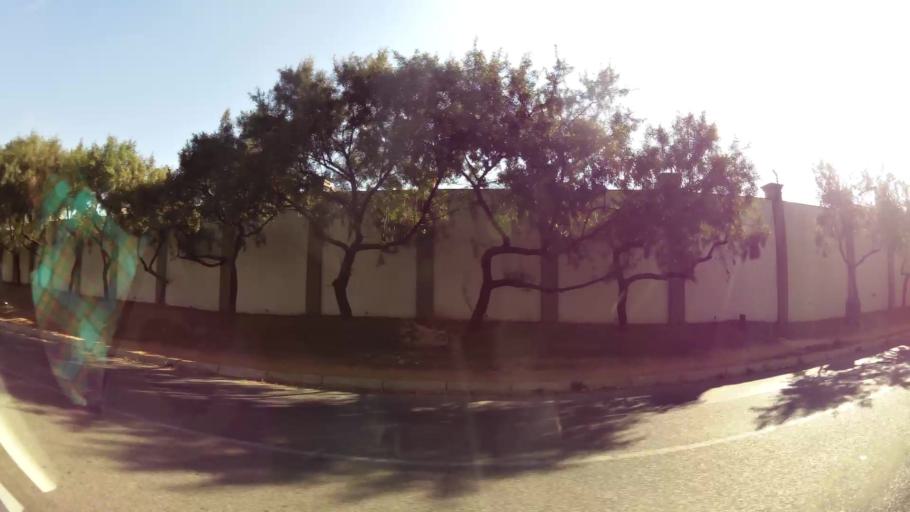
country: ZA
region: Gauteng
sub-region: Ekurhuleni Metropolitan Municipality
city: Germiston
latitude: -26.1675
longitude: 28.1369
